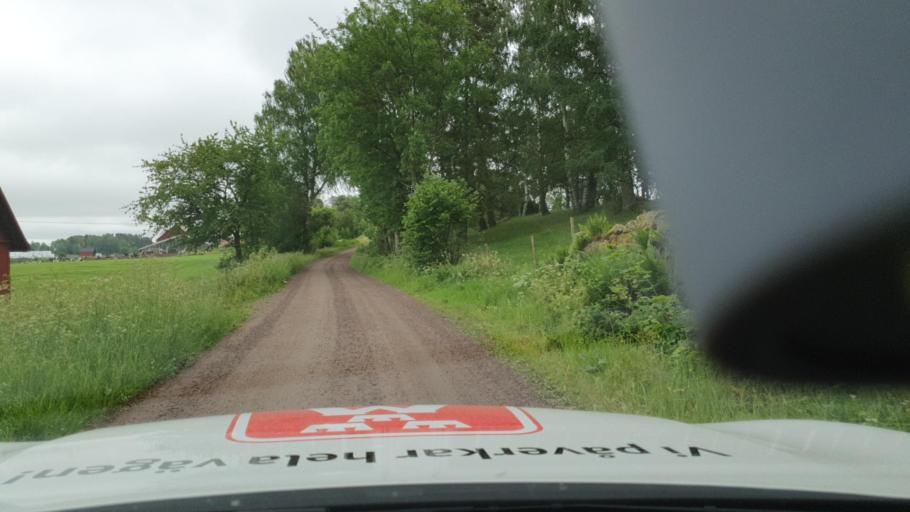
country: SE
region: Vaestra Goetaland
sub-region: Skovde Kommun
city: Stopen
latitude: 58.4003
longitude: 13.9927
